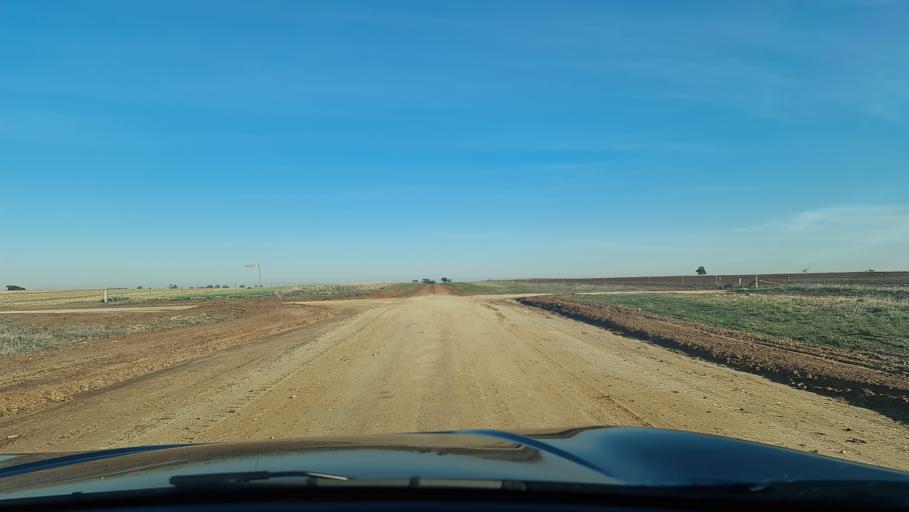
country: AU
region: Victoria
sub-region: Horsham
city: Horsham
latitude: -36.3538
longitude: 142.3951
